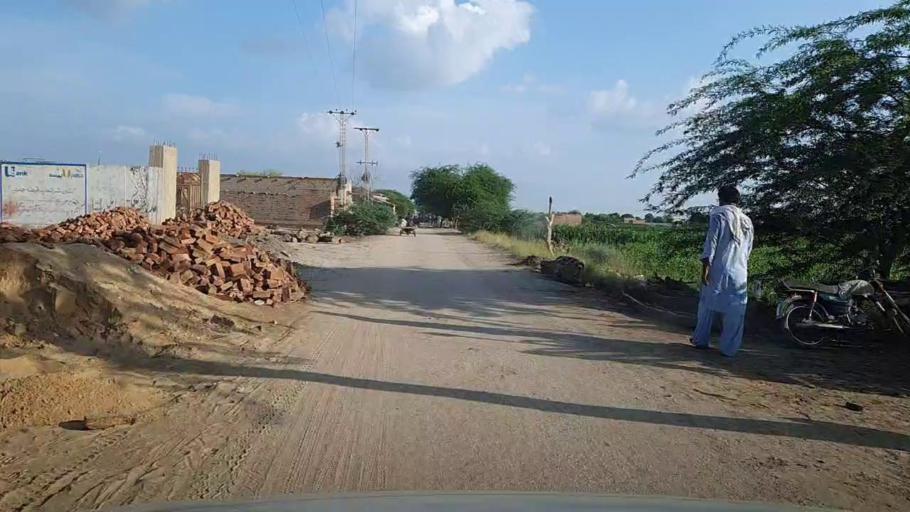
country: PK
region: Sindh
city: Hingorja
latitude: 27.0912
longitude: 68.4171
